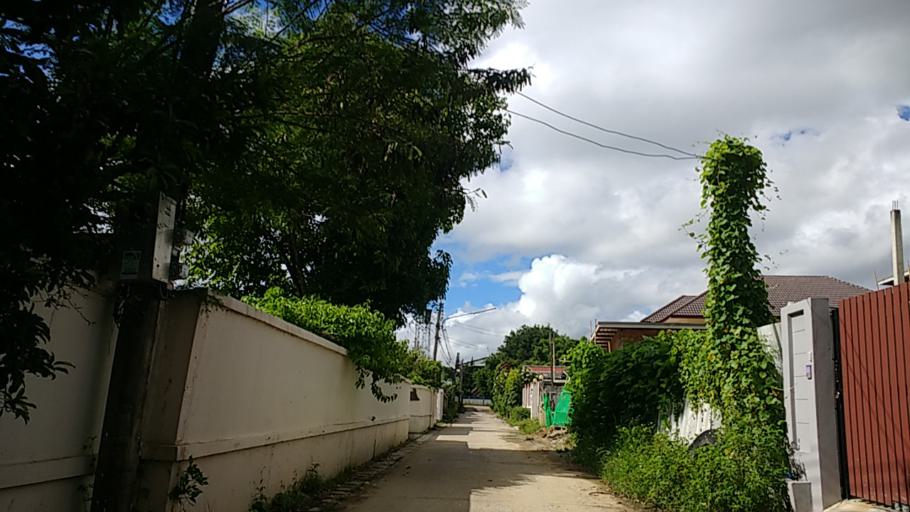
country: TH
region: Chiang Mai
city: Chiang Mai
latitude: 18.7529
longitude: 99.0055
